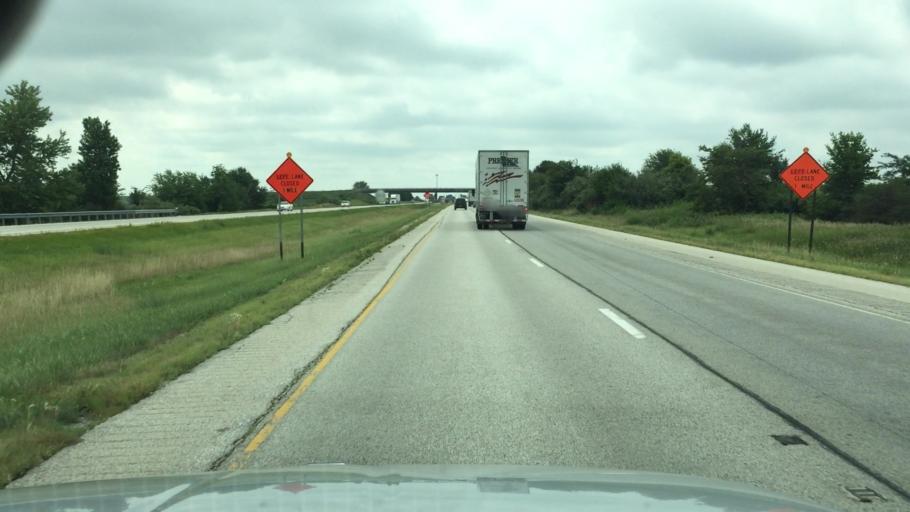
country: US
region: Illinois
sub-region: Knox County
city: Galesburg
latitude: 41.0093
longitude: -90.3351
